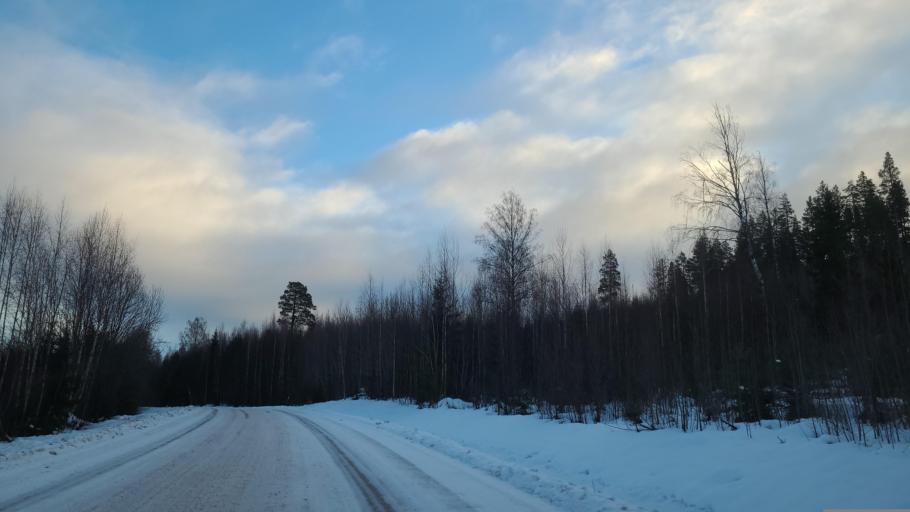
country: SE
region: Gaevleborg
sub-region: Bollnas Kommun
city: Bollnas
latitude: 61.3904
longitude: 16.4630
